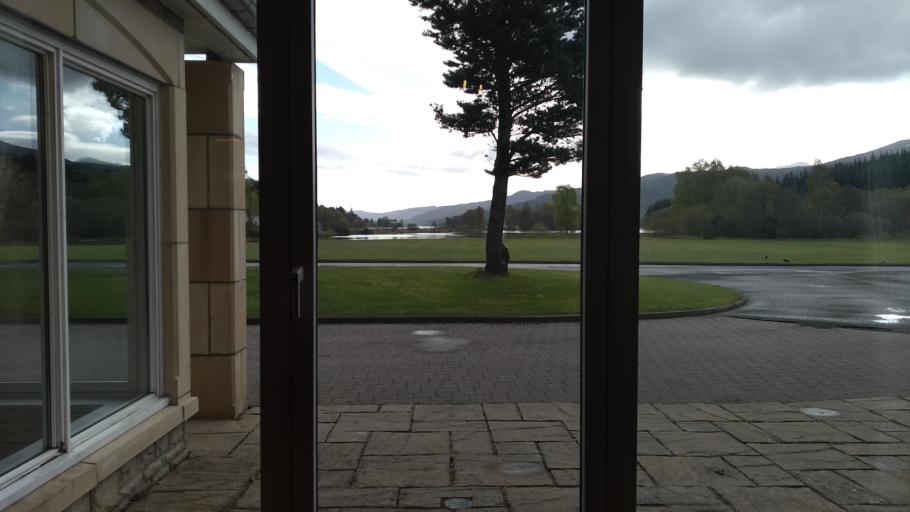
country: GB
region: Scotland
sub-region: Perth and Kinross
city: Aberfeldy
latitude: 56.7063
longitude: -4.0057
